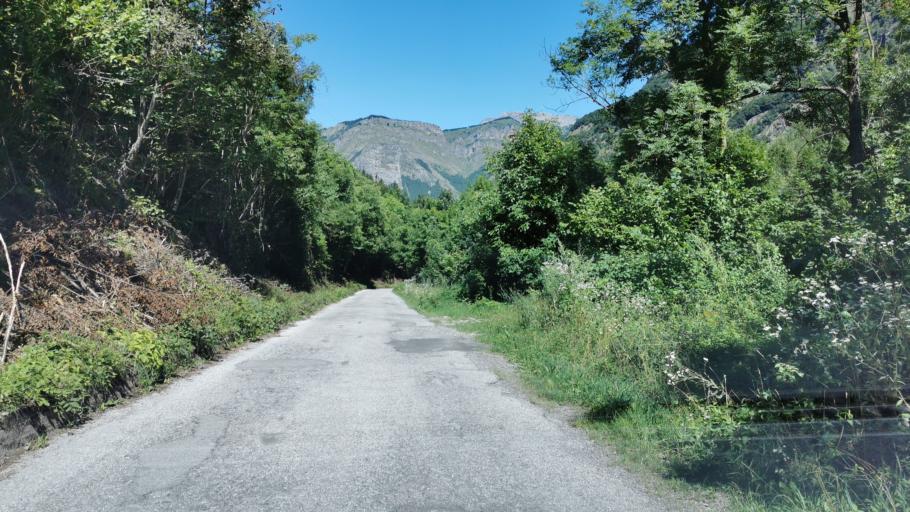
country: IT
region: Piedmont
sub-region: Provincia di Cuneo
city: Entracque
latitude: 44.2127
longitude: 7.3817
